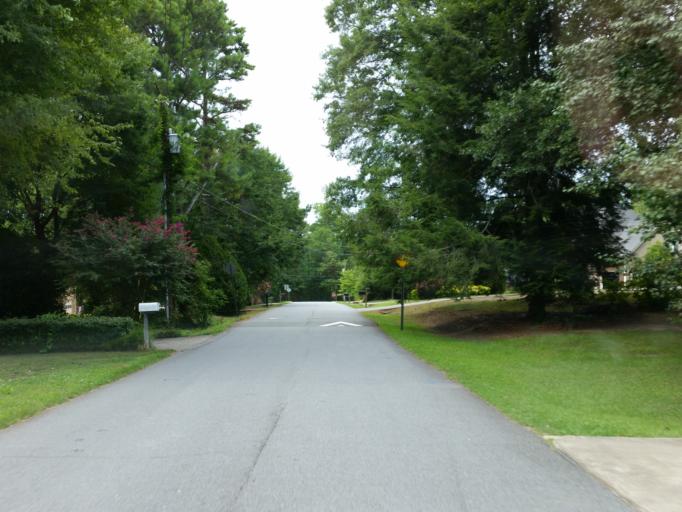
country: US
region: Georgia
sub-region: Cherokee County
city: Woodstock
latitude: 34.0494
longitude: -84.4947
